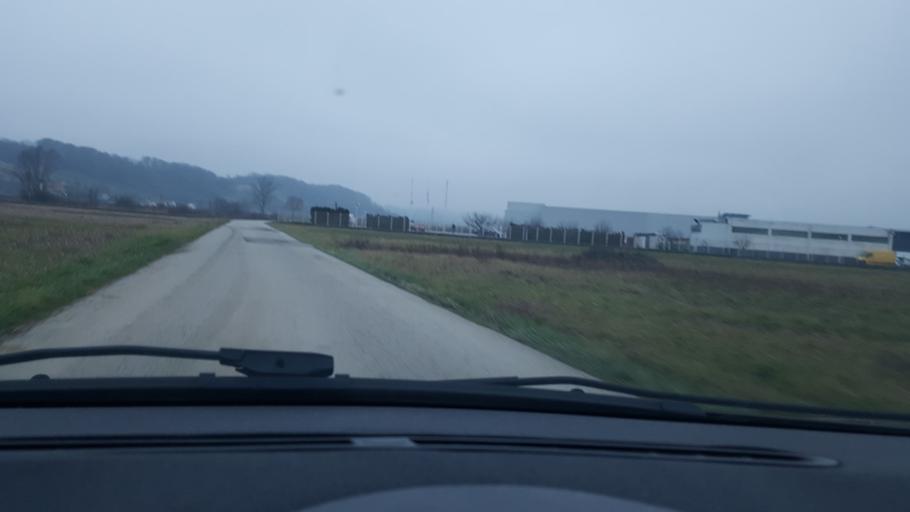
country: HR
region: Krapinsko-Zagorska
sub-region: Grad Krapina
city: Krapina
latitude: 46.1183
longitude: 15.8888
